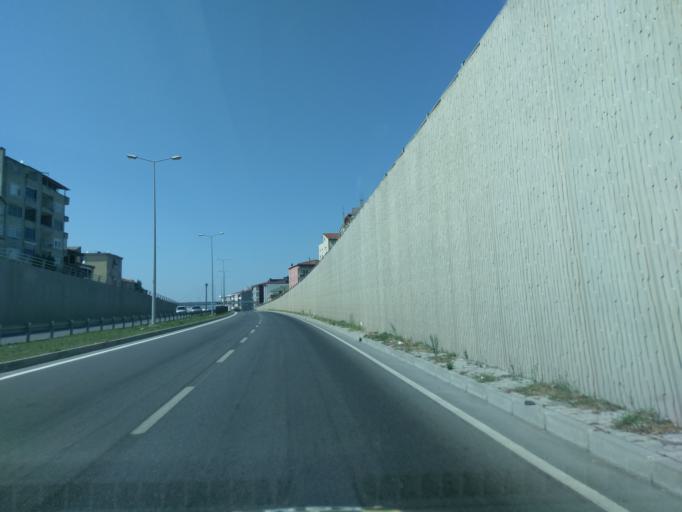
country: TR
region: Samsun
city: Bafra
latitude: 41.5529
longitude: 35.9241
